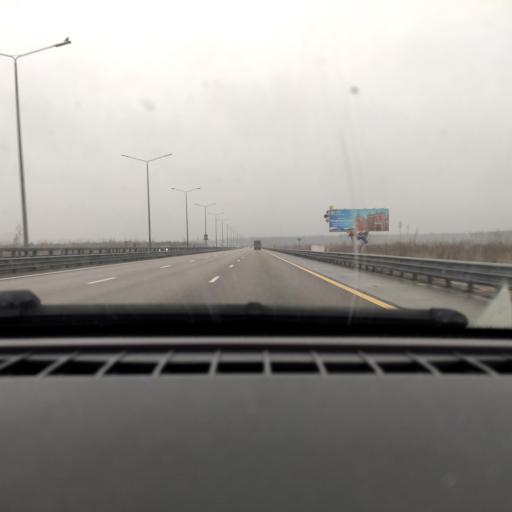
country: RU
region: Voronezj
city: Somovo
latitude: 51.7546
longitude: 39.3070
